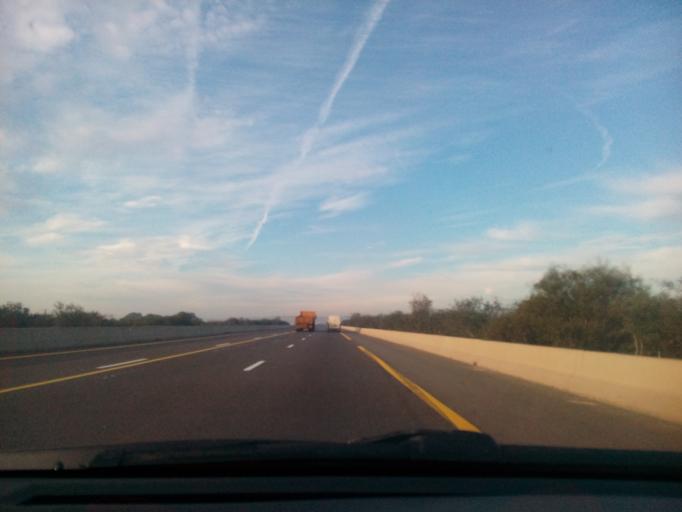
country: DZ
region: Relizane
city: Relizane
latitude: 35.7908
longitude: 0.4272
